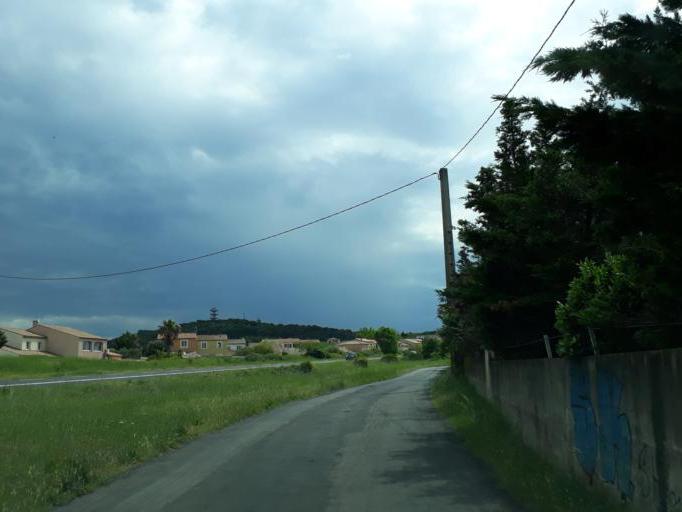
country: FR
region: Languedoc-Roussillon
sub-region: Departement de l'Herault
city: Agde
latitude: 43.2974
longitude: 3.4850
